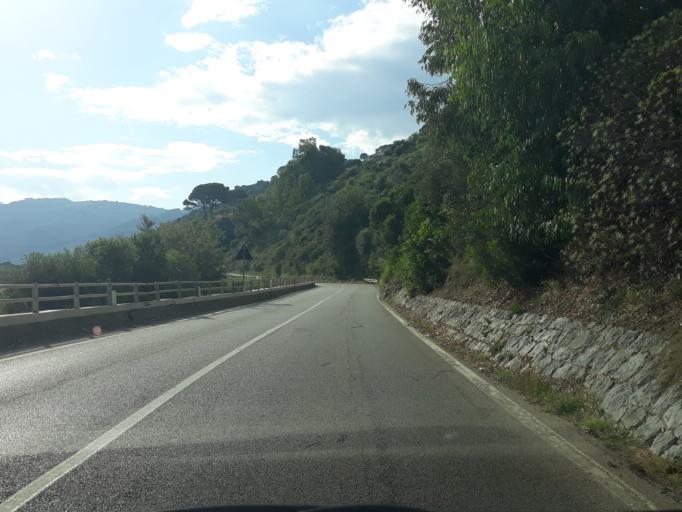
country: IT
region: Sicily
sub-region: Palermo
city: Cefalu
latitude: 38.0289
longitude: 14.0455
